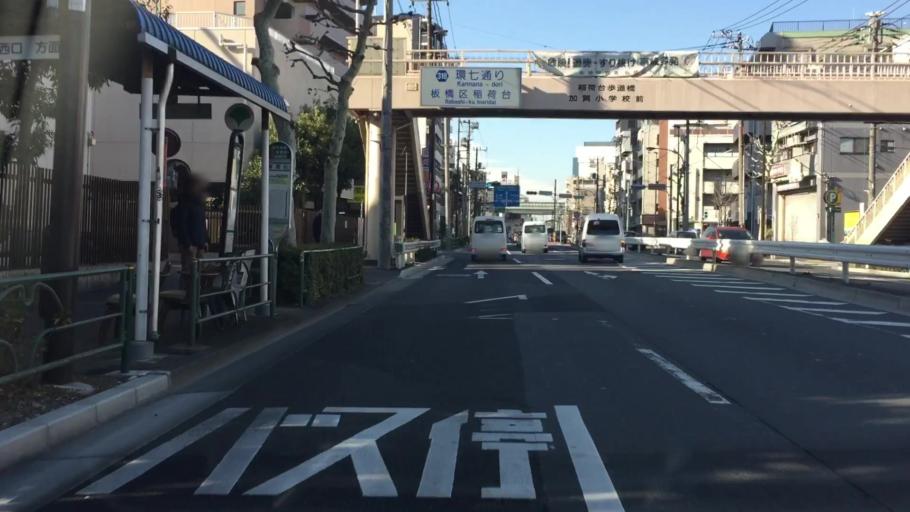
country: JP
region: Saitama
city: Kawaguchi
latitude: 35.7625
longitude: 139.7103
